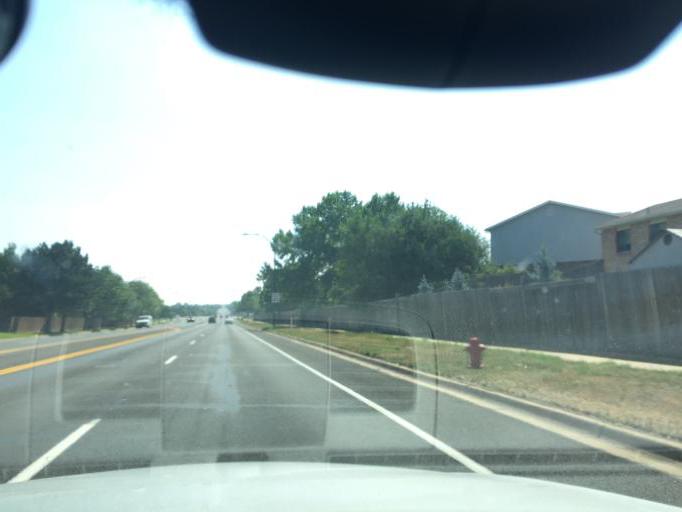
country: US
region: Colorado
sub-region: Broomfield County
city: Broomfield
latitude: 39.8997
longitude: -105.0575
